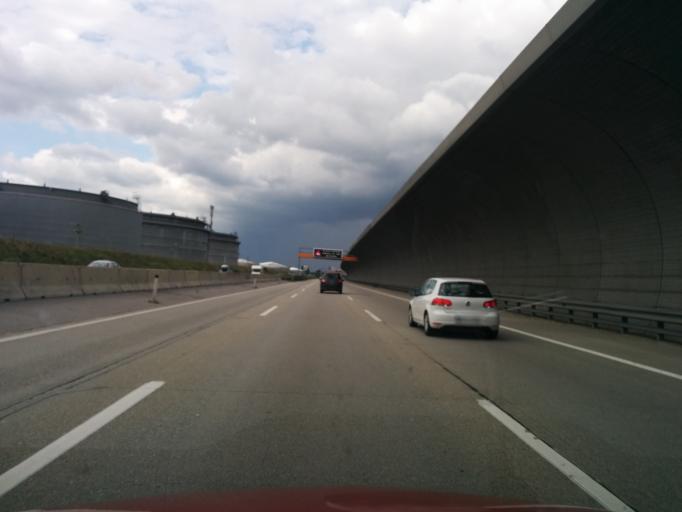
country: AT
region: Lower Austria
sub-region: Politischer Bezirk Wien-Umgebung
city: Schwechat
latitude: 48.1450
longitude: 16.5095
